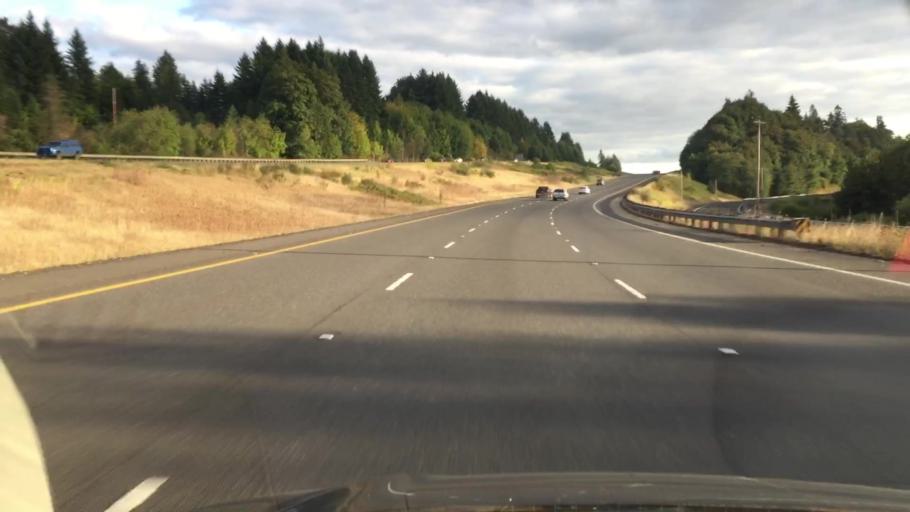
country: US
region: Washington
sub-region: Cowlitz County
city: Castle Rock
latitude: 46.2536
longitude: -122.8841
